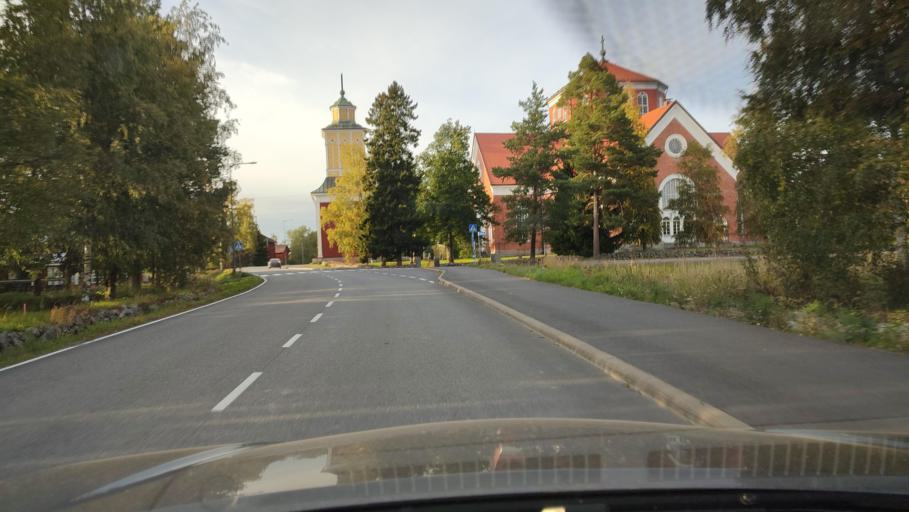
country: FI
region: Ostrobothnia
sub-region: Sydosterbotten
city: Kristinestad
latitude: 62.2457
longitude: 21.5210
